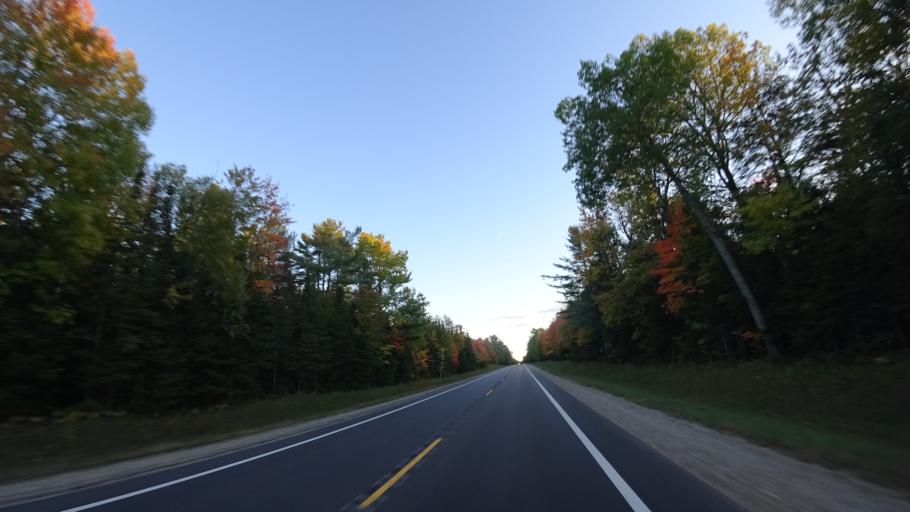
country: US
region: Michigan
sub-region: Mackinac County
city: Saint Ignace
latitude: 46.2701
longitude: -85.0095
